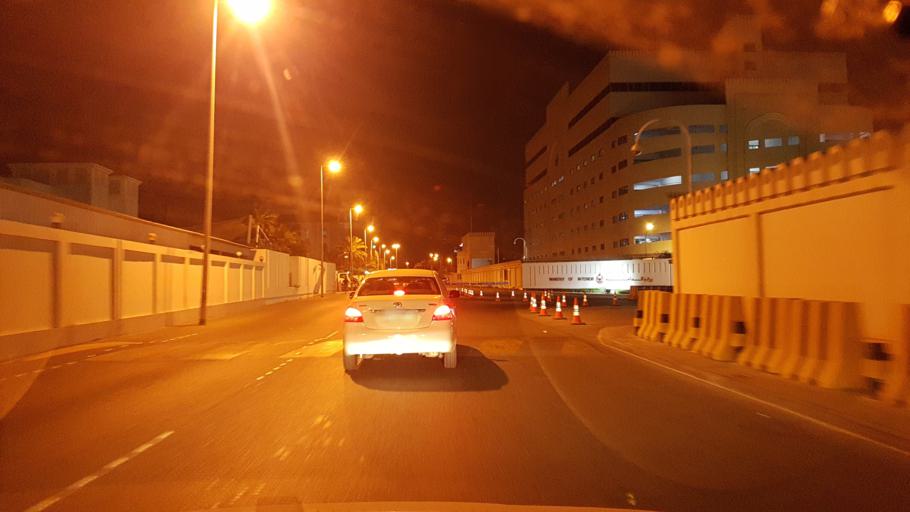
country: BH
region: Manama
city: Manama
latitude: 26.2225
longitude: 50.5778
